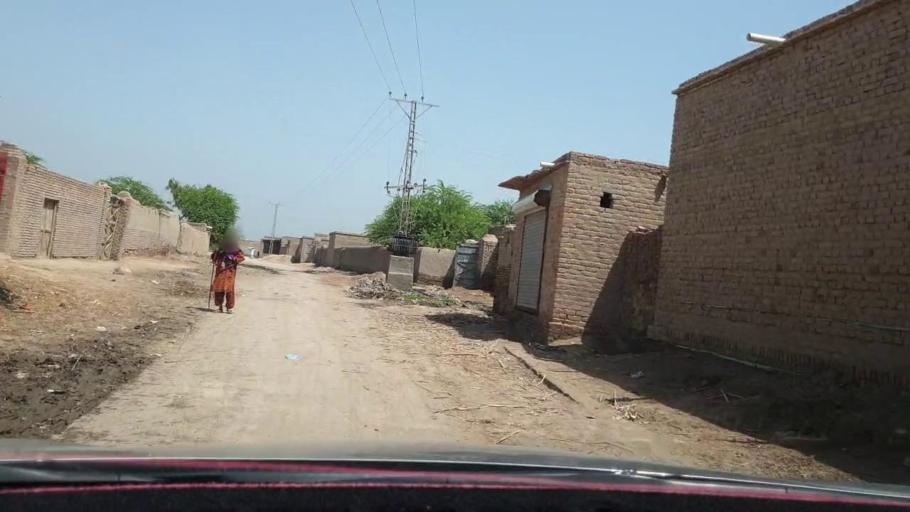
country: PK
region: Sindh
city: Warah
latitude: 27.4419
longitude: 67.7798
